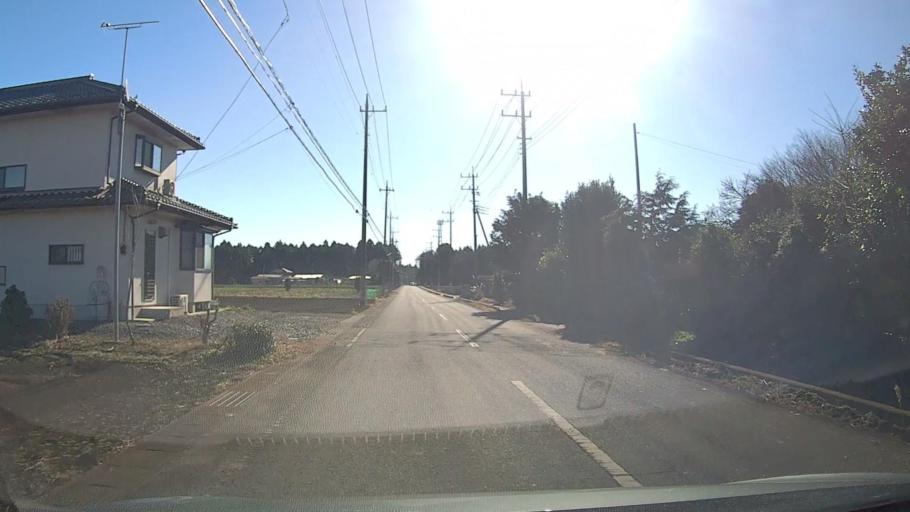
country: JP
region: Ibaraki
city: Mito-shi
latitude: 36.4436
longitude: 140.4400
